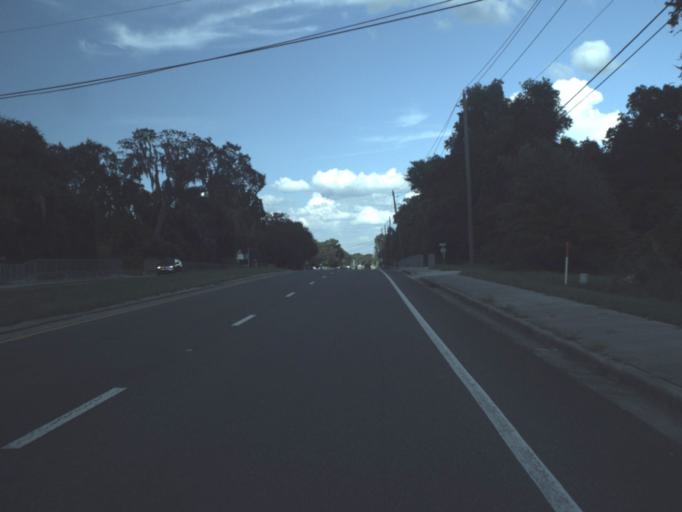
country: US
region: Florida
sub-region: Citrus County
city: Inverness
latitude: 28.8423
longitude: -82.2869
